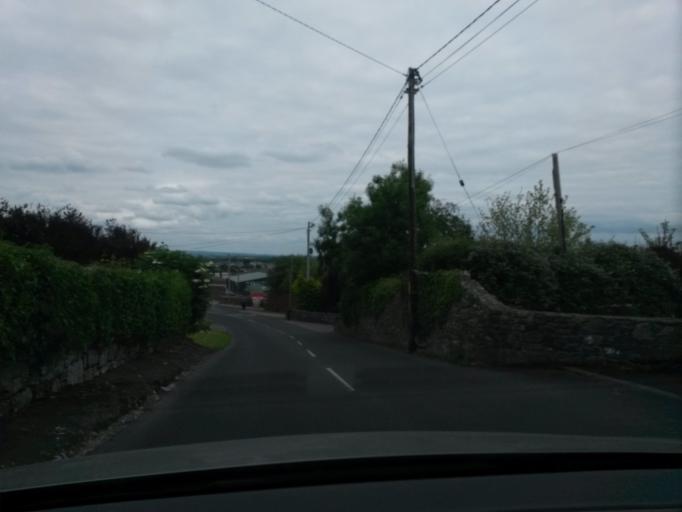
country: IE
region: Munster
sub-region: An Clar
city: Ennis
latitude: 52.8386
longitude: -8.9977
